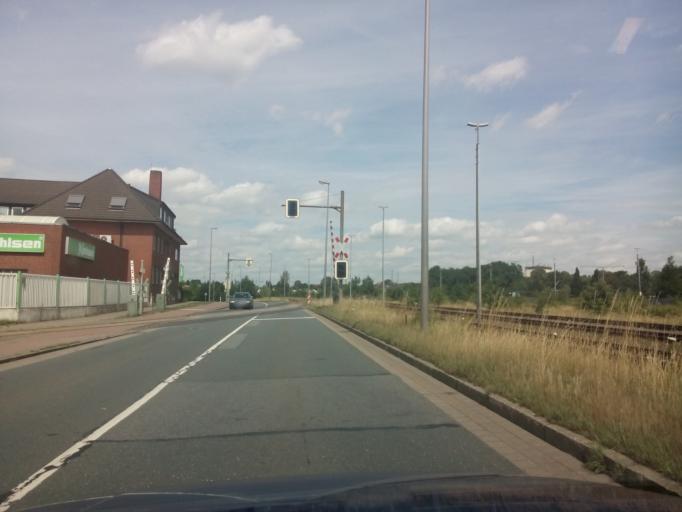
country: DE
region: Lower Saxony
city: Ritterhude
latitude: 53.1171
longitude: 8.7516
